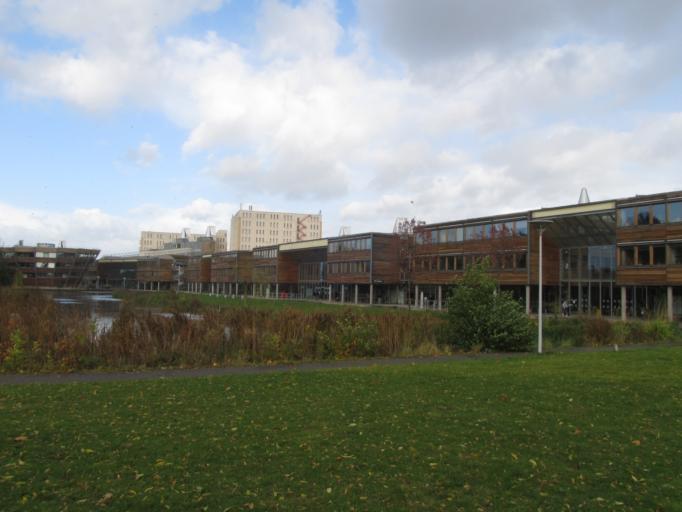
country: GB
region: England
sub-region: Nottingham
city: Nottingham
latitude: 52.9520
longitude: -1.1876
